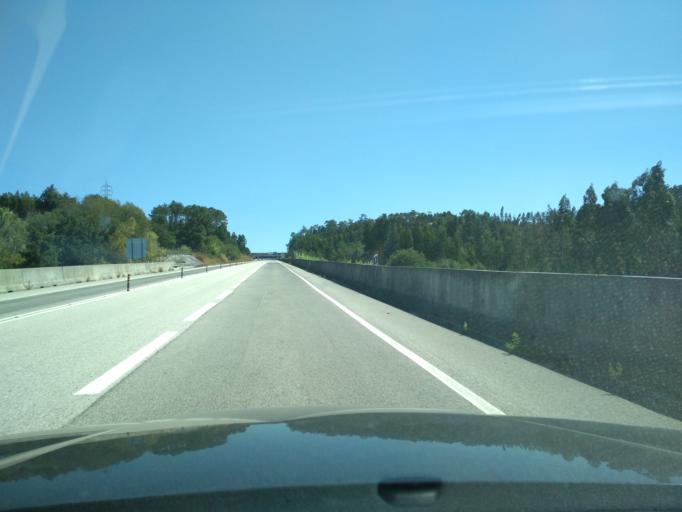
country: PT
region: Leiria
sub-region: Pombal
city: Pombal
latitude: 39.9476
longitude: -8.6809
